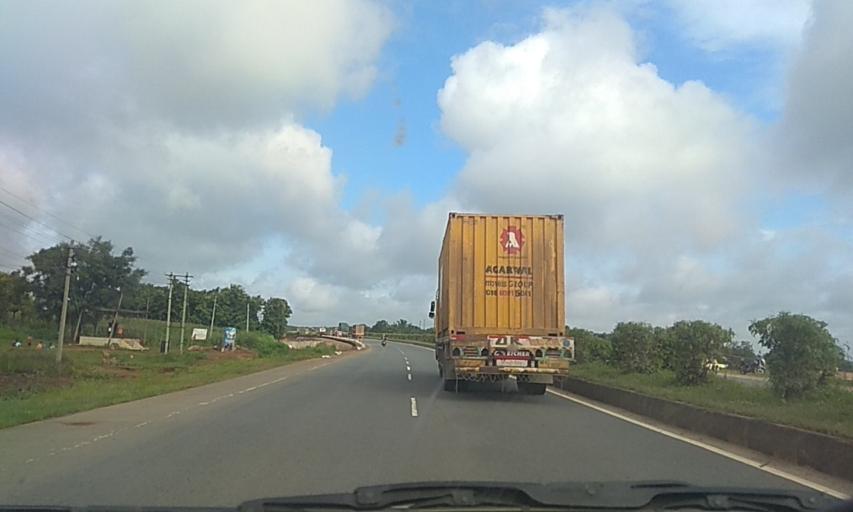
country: IN
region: Karnataka
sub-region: Haveri
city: Shiggaon
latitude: 15.0148
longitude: 75.1901
